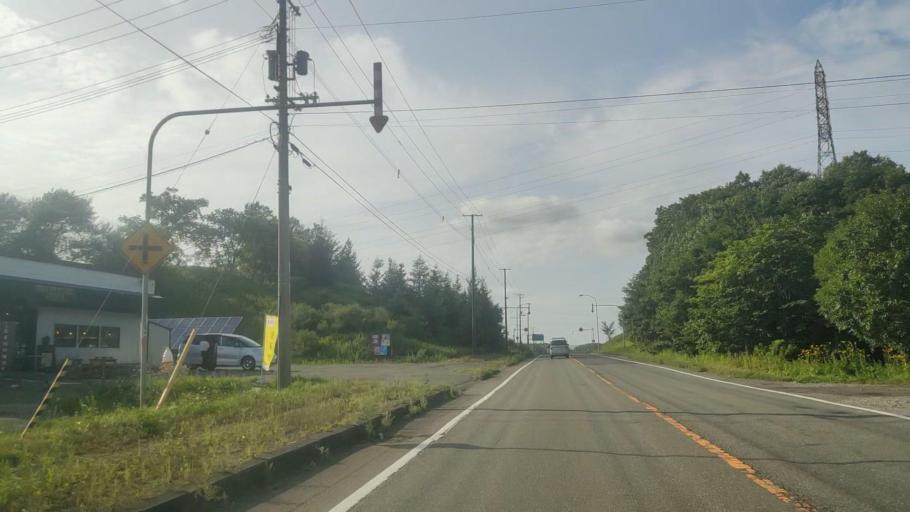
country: JP
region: Hokkaido
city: Chitose
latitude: 42.8818
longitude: 141.8141
